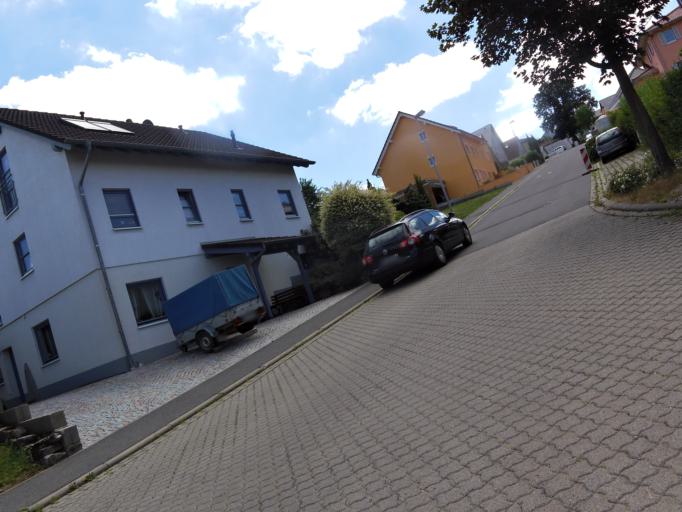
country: DE
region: Bavaria
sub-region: Regierungsbezirk Unterfranken
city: Kist
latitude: 49.7463
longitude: 9.8374
